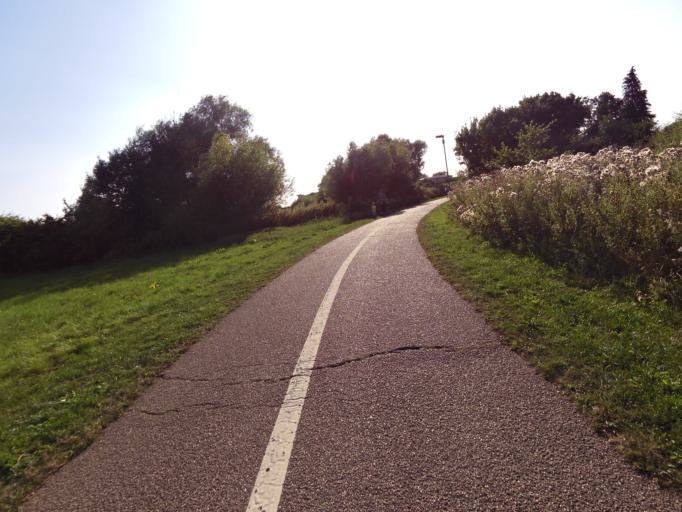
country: GB
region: England
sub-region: Essex
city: Chelmsford
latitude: 51.7300
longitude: 0.4892
